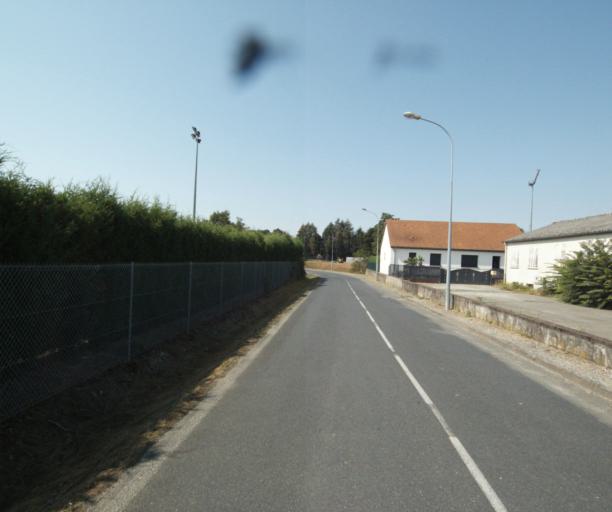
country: FR
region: Bourgogne
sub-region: Departement de Saone-et-Loire
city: Gueugnon
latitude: 46.5948
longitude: 4.0583
